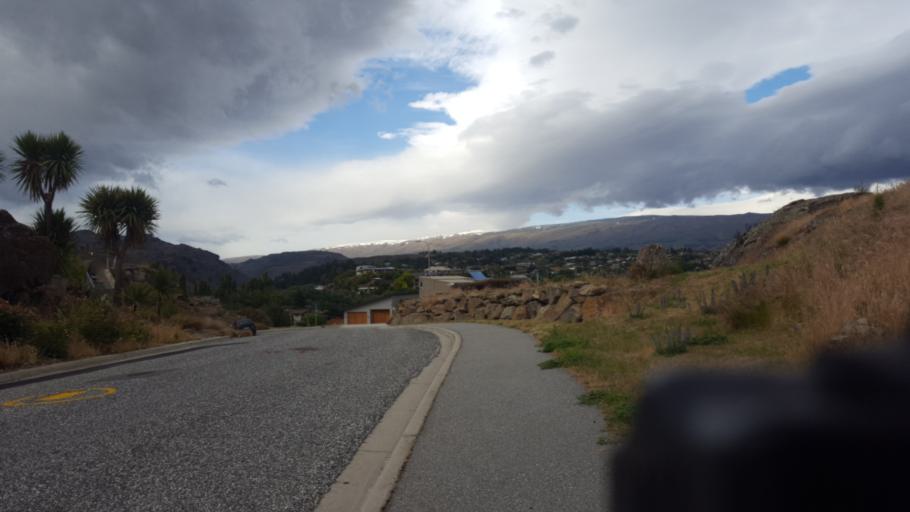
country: NZ
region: Otago
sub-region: Queenstown-Lakes District
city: Wanaka
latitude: -45.2534
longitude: 169.4009
